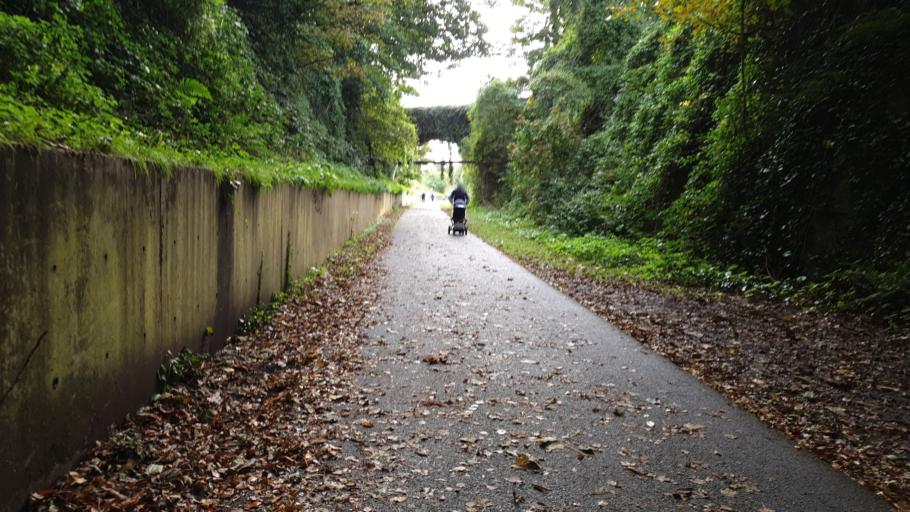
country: IE
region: Munster
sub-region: County Cork
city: Cork
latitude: 51.8971
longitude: -8.4202
